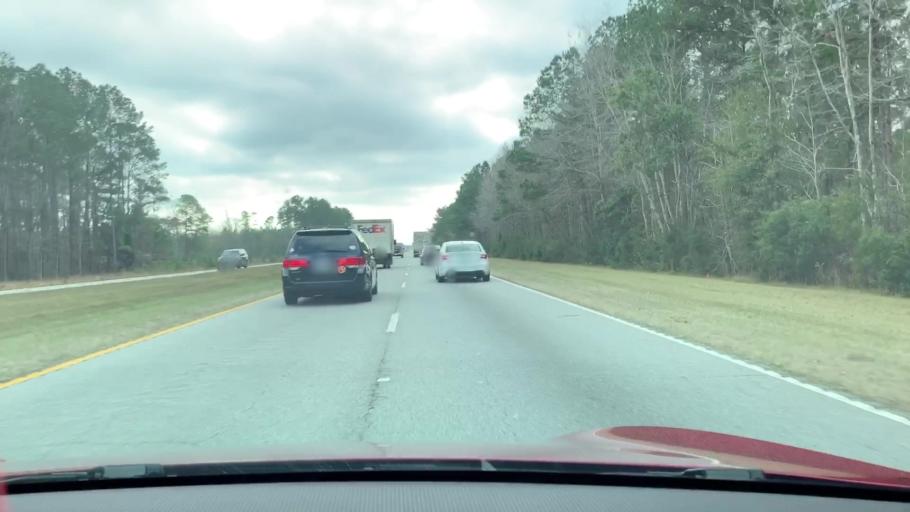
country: US
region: South Carolina
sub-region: Jasper County
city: Hardeeville
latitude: 32.2503
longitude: -81.0775
